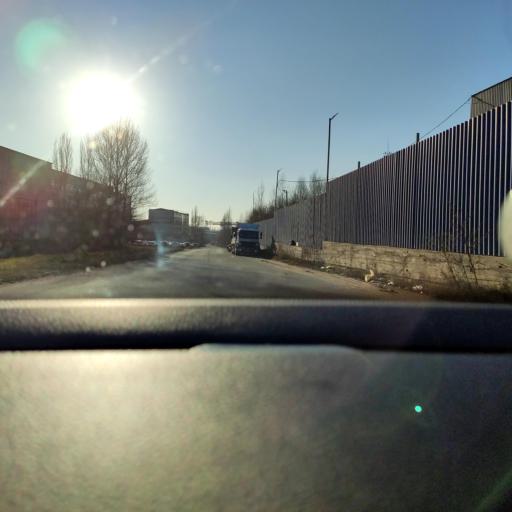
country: RU
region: Moskovskaya
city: Kotel'niki
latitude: 55.6343
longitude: 37.8260
